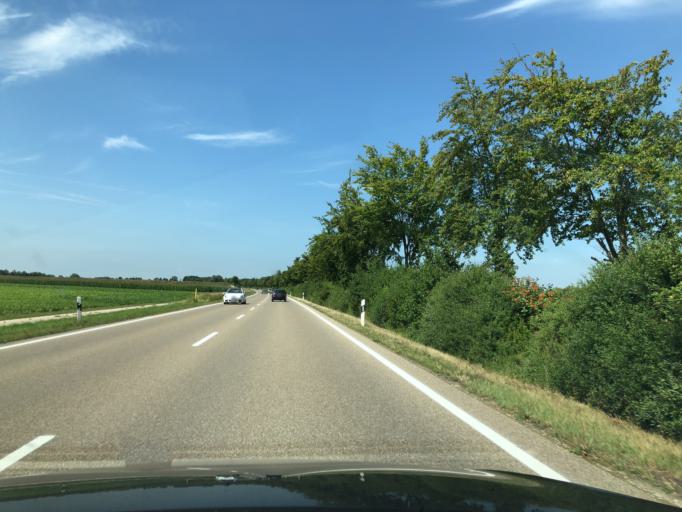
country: DE
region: Bavaria
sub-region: Swabia
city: Niederschonenfeld
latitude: 48.7098
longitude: 10.9626
